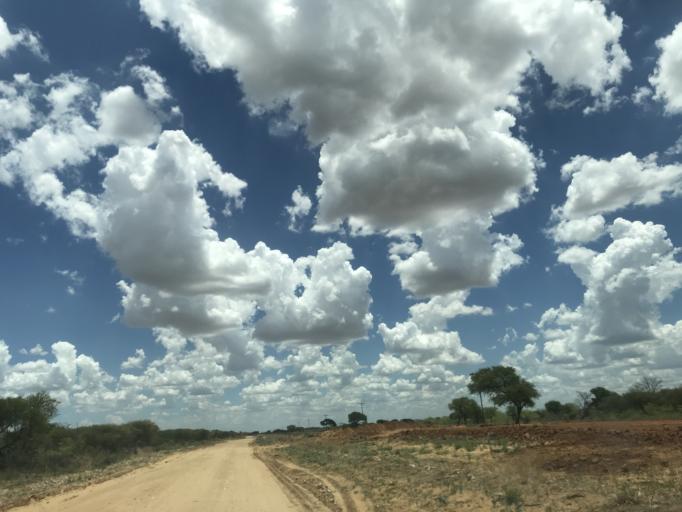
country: BW
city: Mabuli
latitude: -25.7922
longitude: 24.6588
